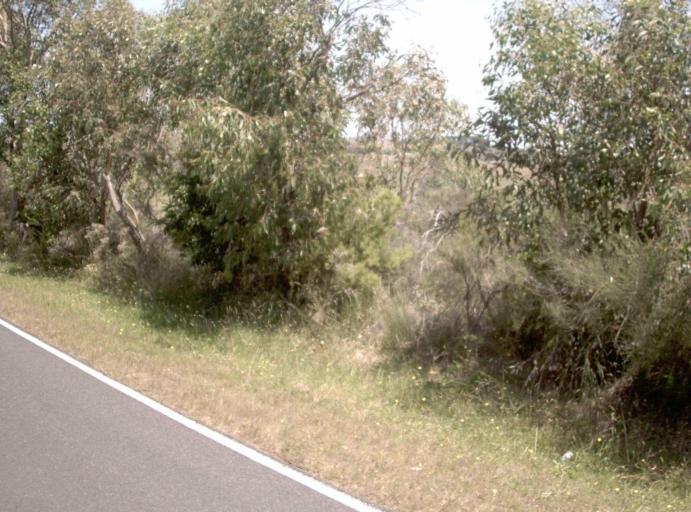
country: AU
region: Victoria
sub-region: Bass Coast
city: North Wonthaggi
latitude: -38.5818
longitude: 145.9832
